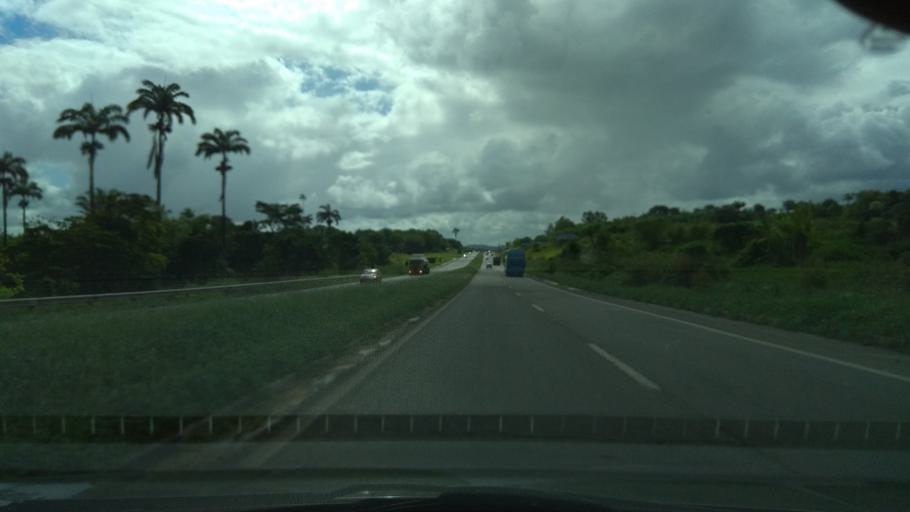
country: BR
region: Bahia
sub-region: Simoes Filho
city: Simoes Filho
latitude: -12.7764
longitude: -38.4173
